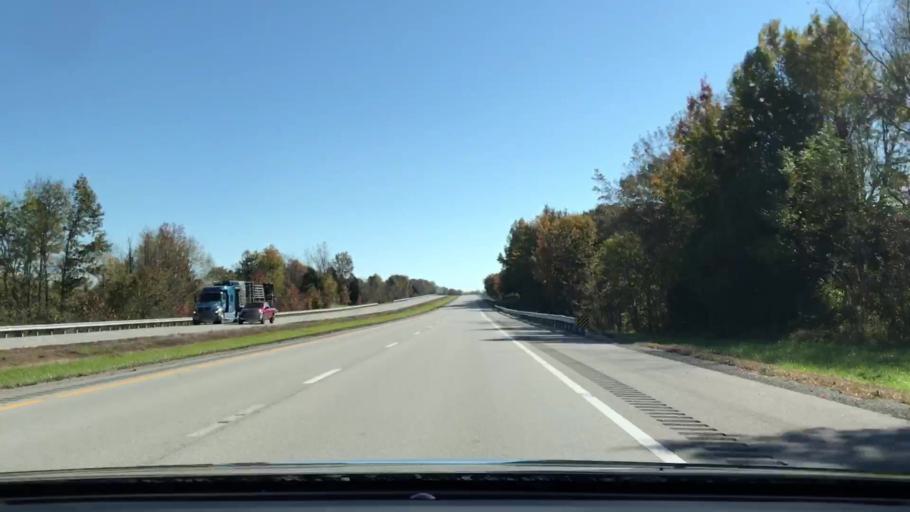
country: US
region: Kentucky
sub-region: Barren County
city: Cave City
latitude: 37.0485
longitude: -86.0870
